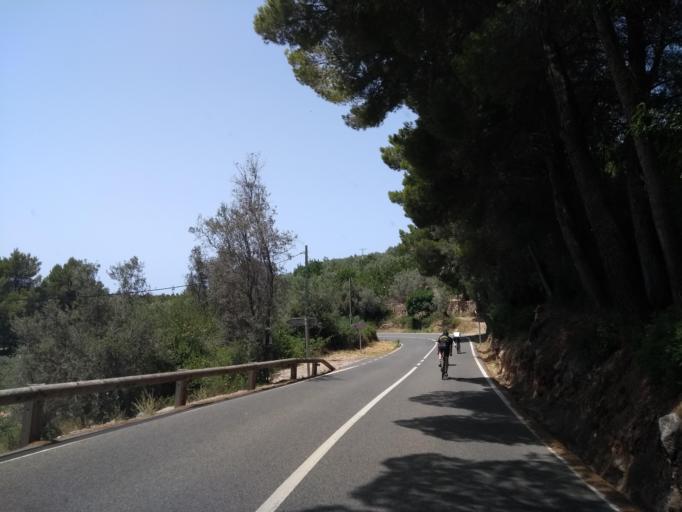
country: ES
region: Balearic Islands
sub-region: Illes Balears
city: Soller
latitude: 39.7789
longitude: 2.7217
